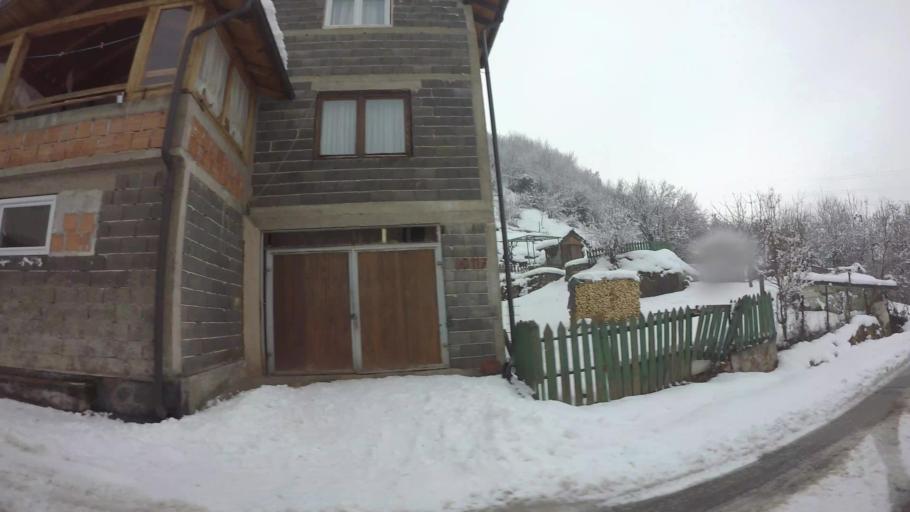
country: BA
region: Federation of Bosnia and Herzegovina
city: Kobilja Glava
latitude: 43.8479
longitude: 18.4105
